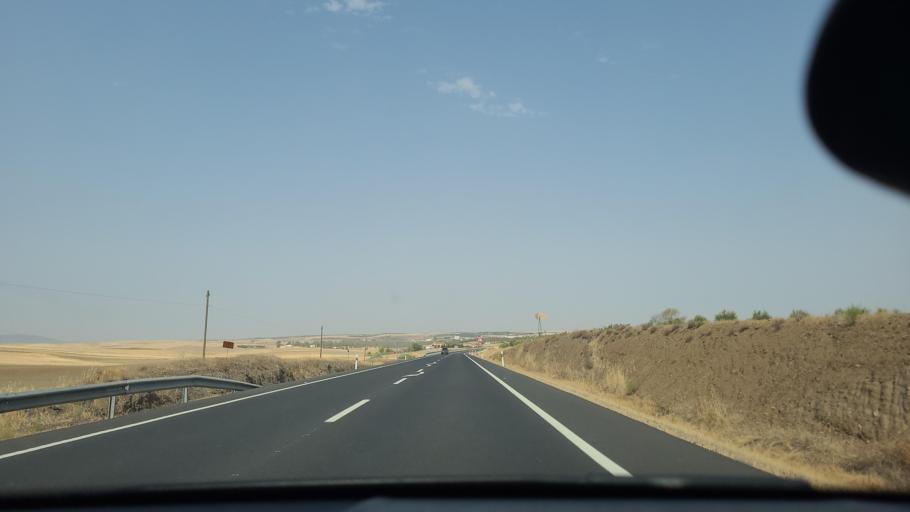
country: ES
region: Extremadura
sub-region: Provincia de Badajoz
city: Berlanga
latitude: 38.2674
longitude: -5.7853
